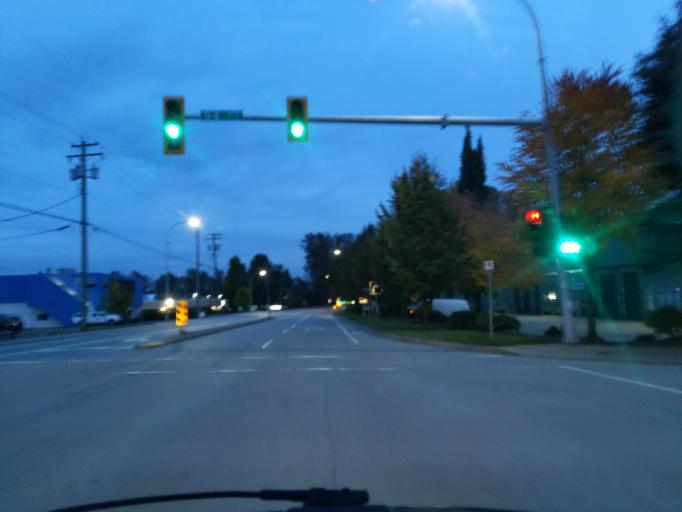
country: CA
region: British Columbia
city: Pitt Meadows
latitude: 49.1734
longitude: -122.6907
